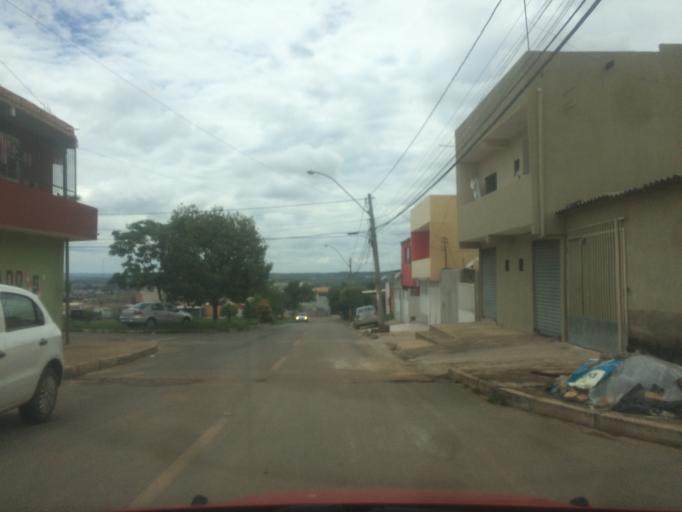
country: BR
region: Federal District
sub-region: Brasilia
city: Brasilia
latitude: -15.9018
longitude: -47.7881
